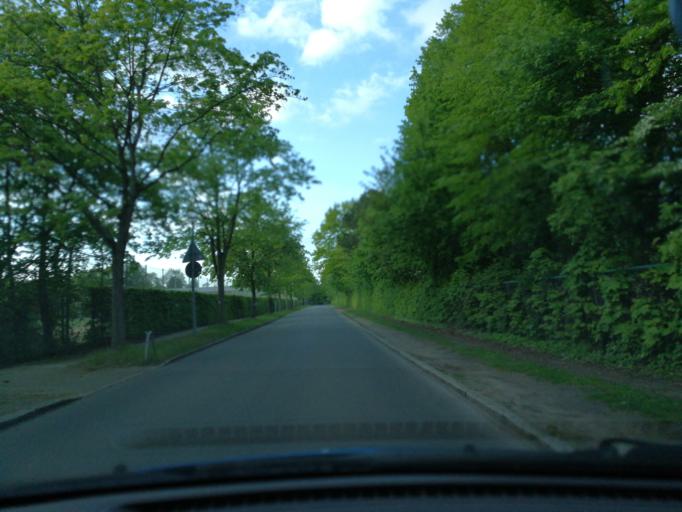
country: DE
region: Lower Saxony
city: Uelzen
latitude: 52.9683
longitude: 10.5652
